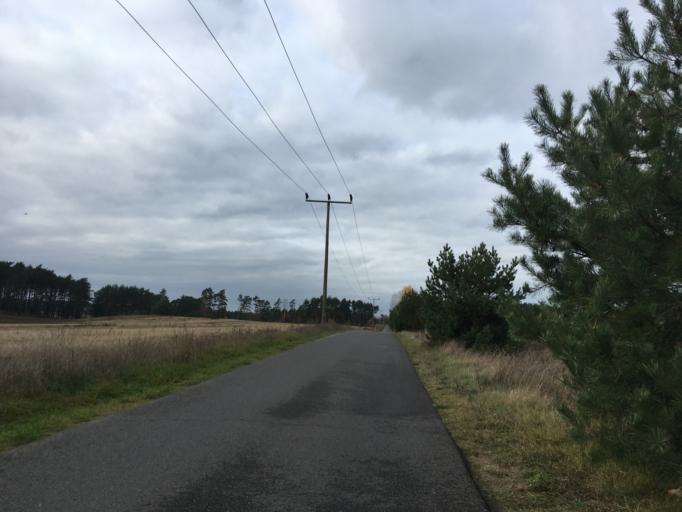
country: DE
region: Brandenburg
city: Jamlitz
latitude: 52.0821
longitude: 14.4487
